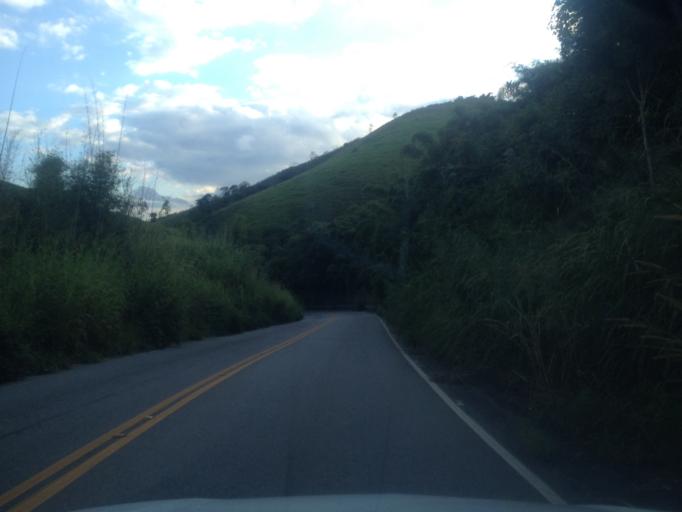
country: BR
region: Rio de Janeiro
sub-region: Quatis
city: Quatis
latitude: -22.3831
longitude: -44.2632
